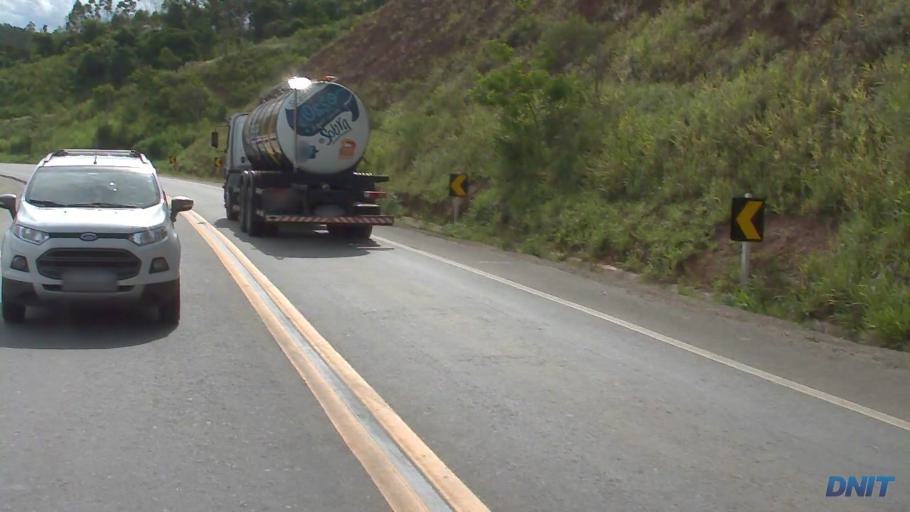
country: BR
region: Minas Gerais
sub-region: Belo Oriente
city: Belo Oriente
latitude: -19.2674
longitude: -42.3540
